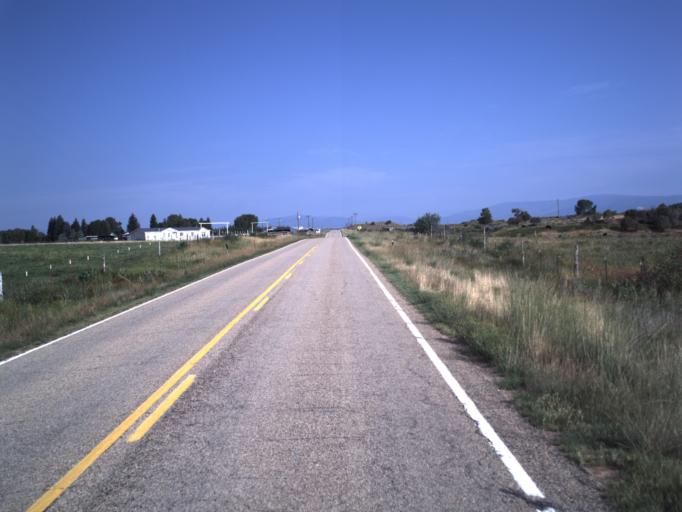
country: US
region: Utah
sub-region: Duchesne County
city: Duchesne
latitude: 40.3091
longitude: -110.2453
